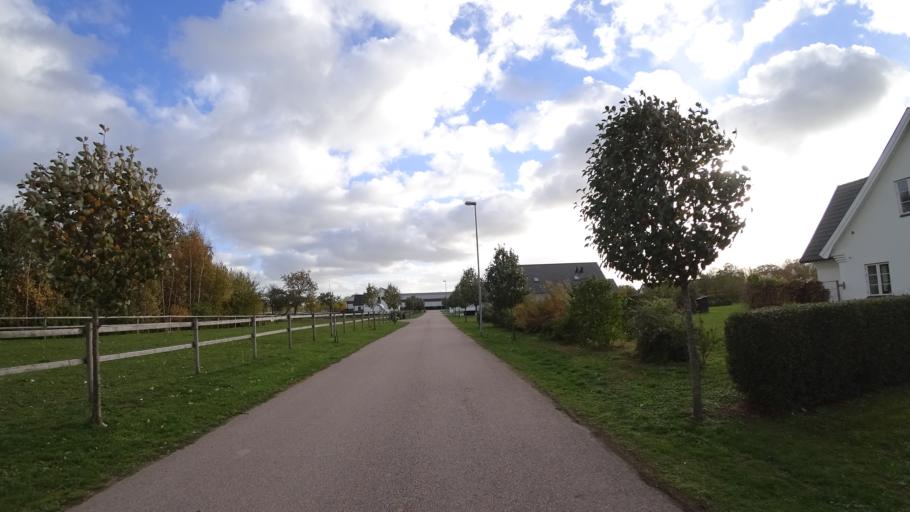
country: SE
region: Skane
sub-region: Staffanstorps Kommun
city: Staffanstorp
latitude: 55.6245
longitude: 13.2135
